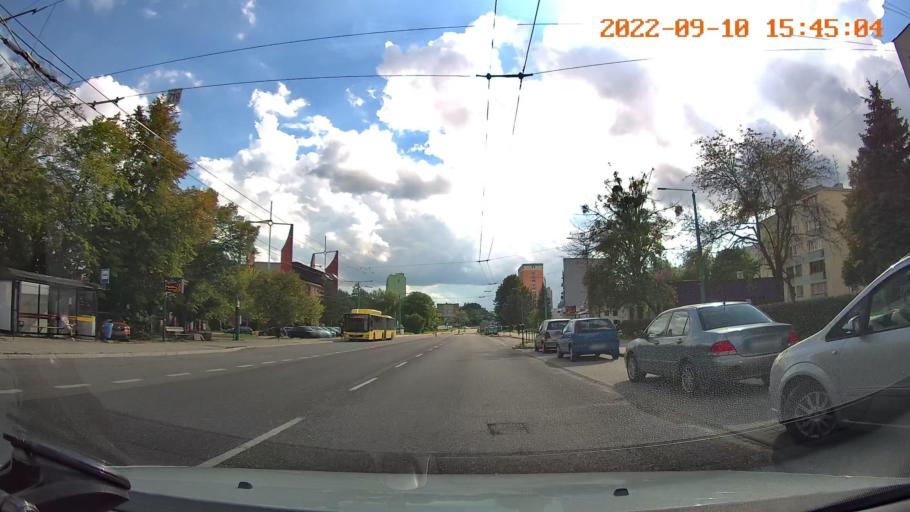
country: PL
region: Silesian Voivodeship
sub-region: Tychy
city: Cielmice
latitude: 50.1137
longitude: 19.0051
